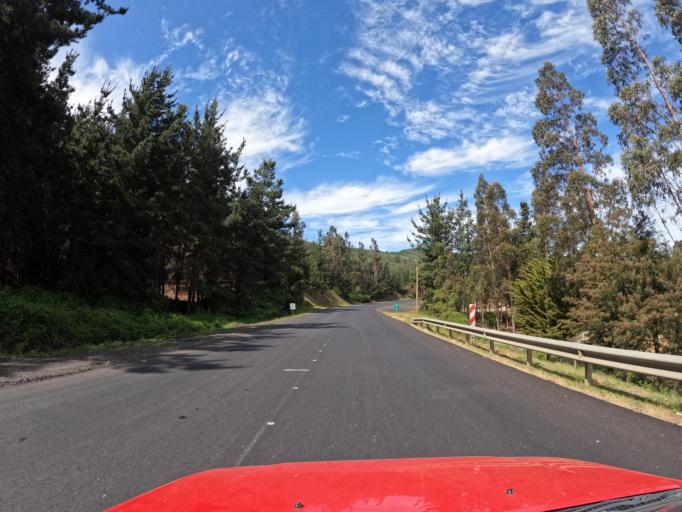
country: CL
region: Maule
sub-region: Provincia de Talca
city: Constitucion
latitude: -35.0438
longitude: -72.0559
